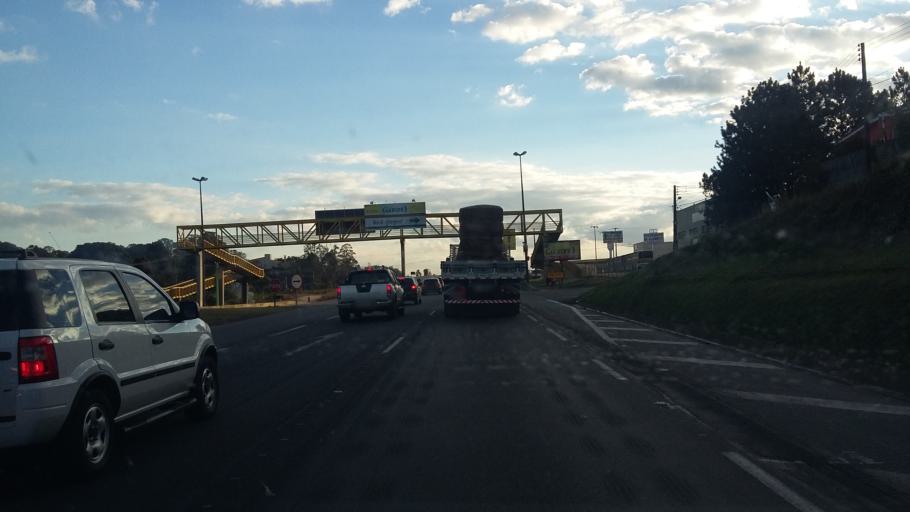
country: BR
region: Parana
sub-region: Campo Largo
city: Campo Largo
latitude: -25.4329
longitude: -49.4041
